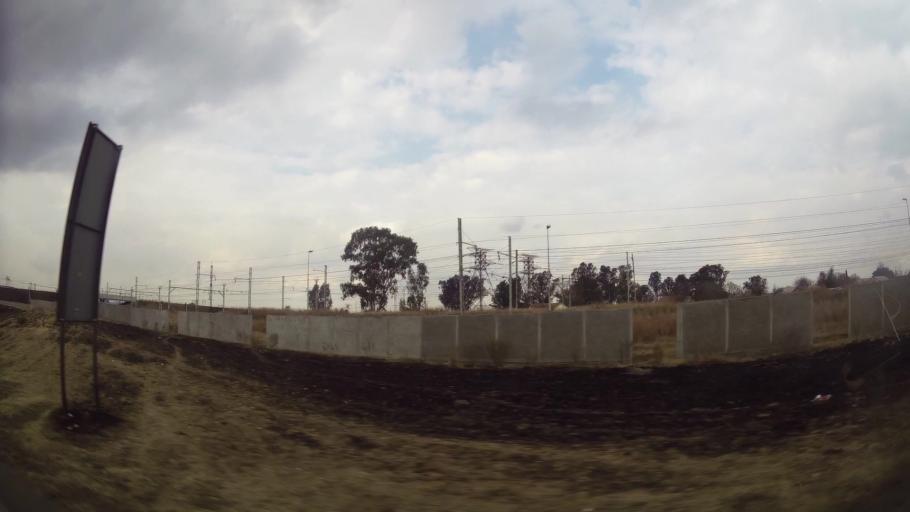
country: ZA
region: Orange Free State
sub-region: Fezile Dabi District Municipality
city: Sasolburg
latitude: -26.8440
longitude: 27.8720
